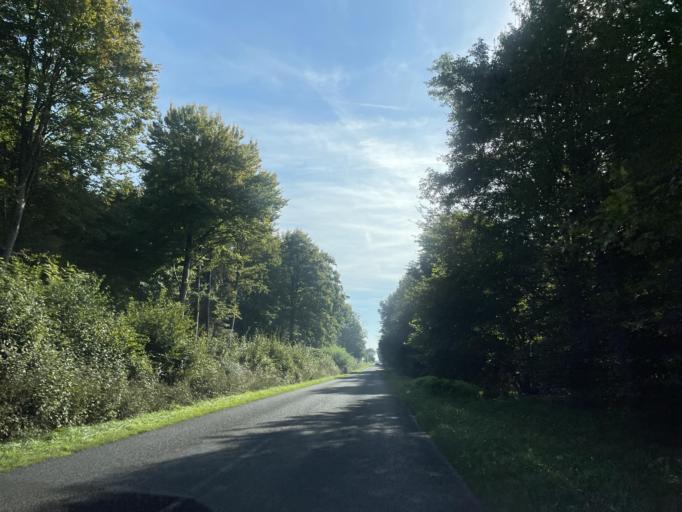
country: FR
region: Ile-de-France
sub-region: Departement de Seine-et-Marne
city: Saint-Jean-les-Deux-Jumeaux
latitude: 48.9141
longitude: 3.0151
